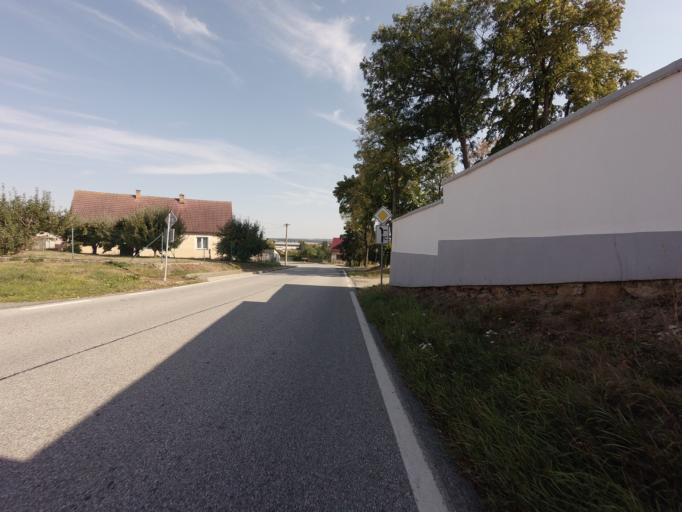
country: CZ
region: Jihocesky
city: Tyn nad Vltavou
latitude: 49.2924
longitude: 14.3908
